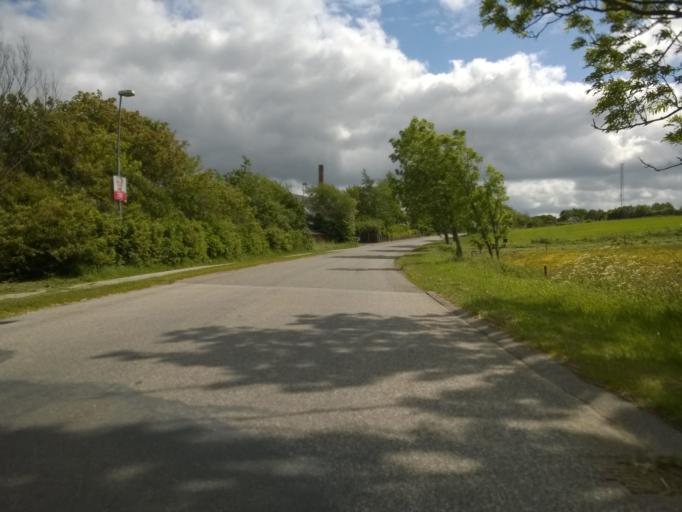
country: DK
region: Central Jutland
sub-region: Holstebro Kommune
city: Vinderup
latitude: 56.4539
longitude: 8.8690
